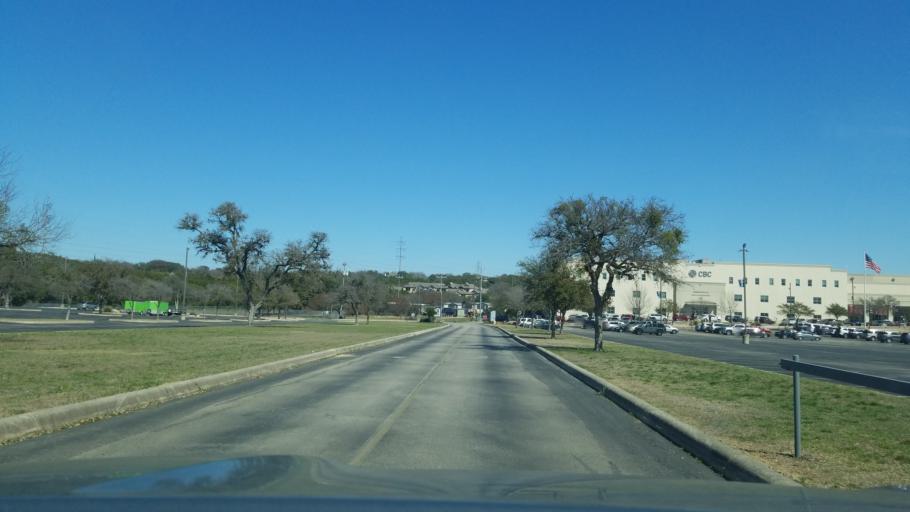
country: US
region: Texas
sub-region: Bexar County
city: Hollywood Park
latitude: 29.6083
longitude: -98.4552
